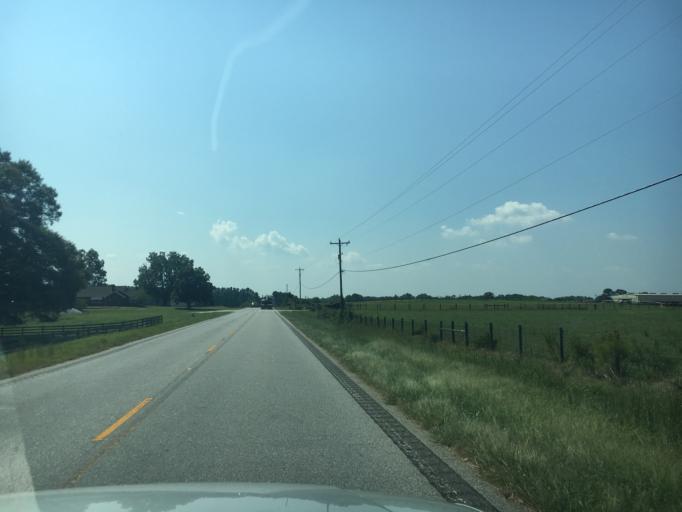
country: US
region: South Carolina
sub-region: Anderson County
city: Centerville
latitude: 34.4967
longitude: -82.7756
